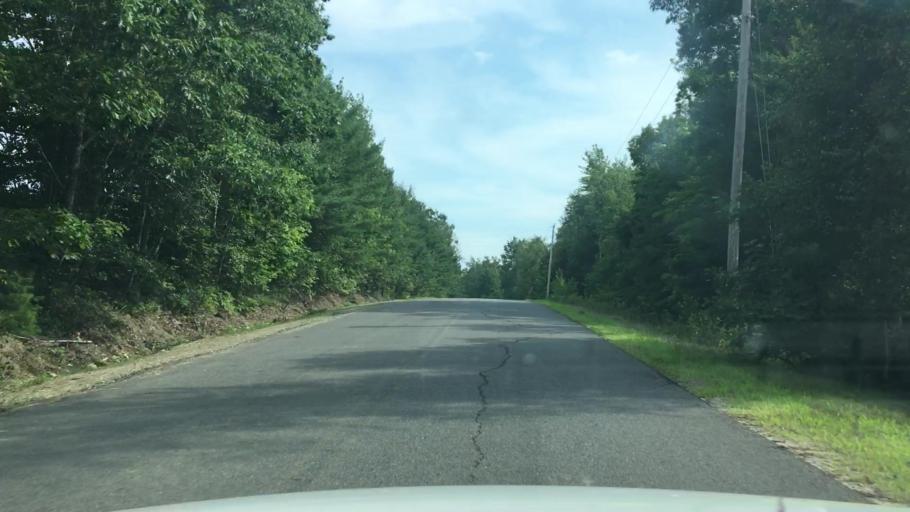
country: US
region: Maine
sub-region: Lincoln County
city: Jefferson
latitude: 44.2423
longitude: -69.4456
